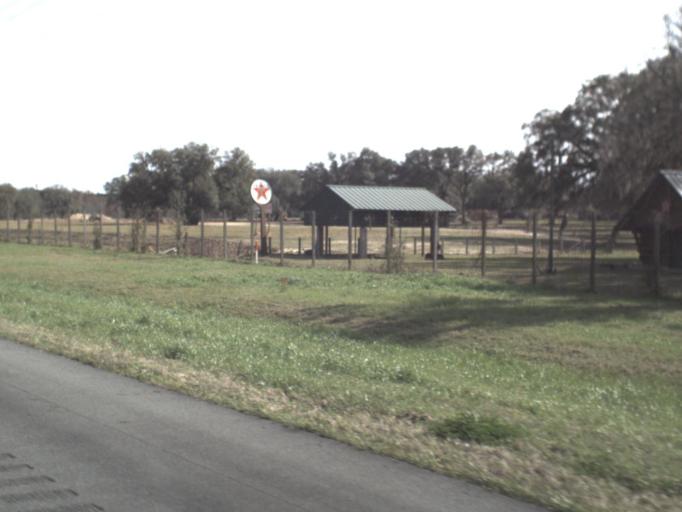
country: US
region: Florida
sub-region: Leon County
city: Tallahassee
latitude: 30.4911
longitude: -84.1676
